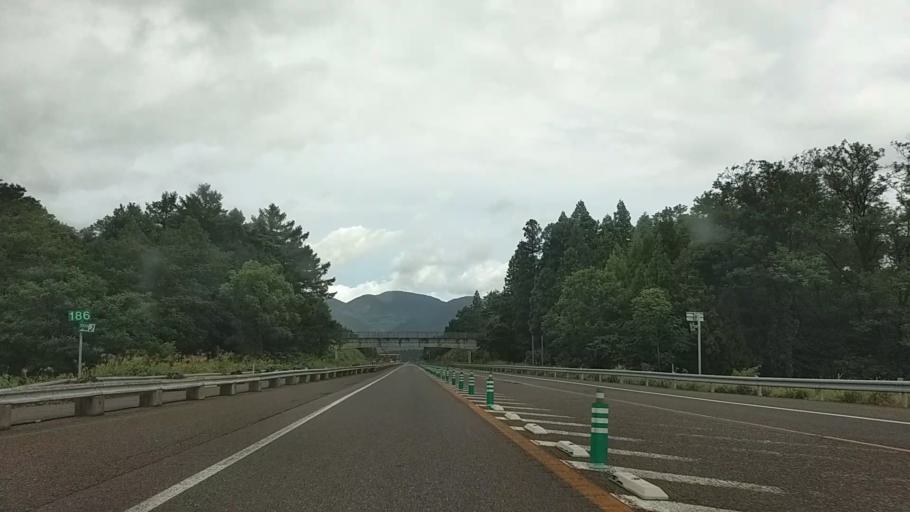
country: JP
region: Niigata
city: Arai
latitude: 36.9819
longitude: 138.2173
